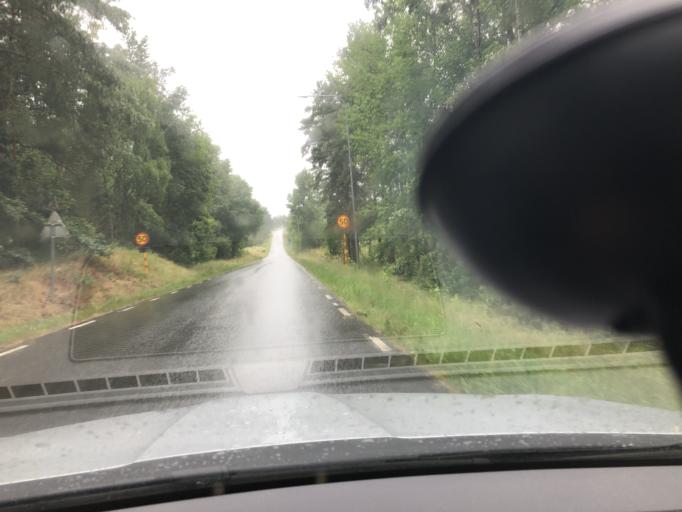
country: SE
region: Blekinge
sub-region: Olofstroms Kommun
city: Jamshog
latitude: 56.1847
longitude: 14.6104
